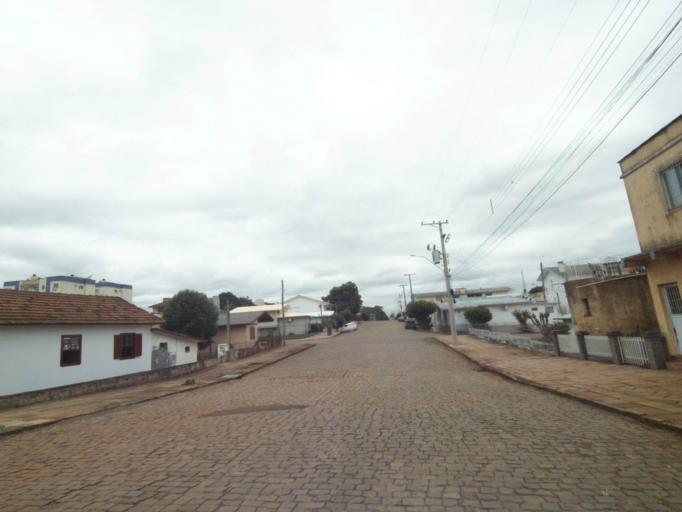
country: BR
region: Rio Grande do Sul
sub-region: Lagoa Vermelha
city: Lagoa Vermelha
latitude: -28.2050
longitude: -51.5267
